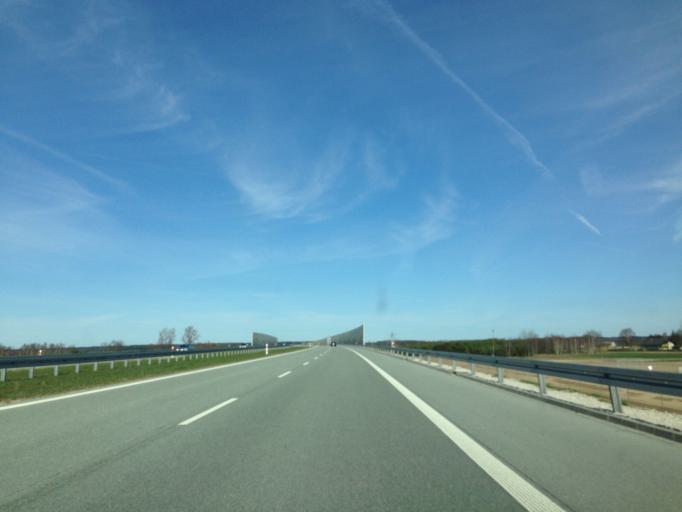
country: PL
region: Lodz Voivodeship
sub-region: Powiat sieradzki
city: Sieradz
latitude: 51.5716
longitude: 18.7861
